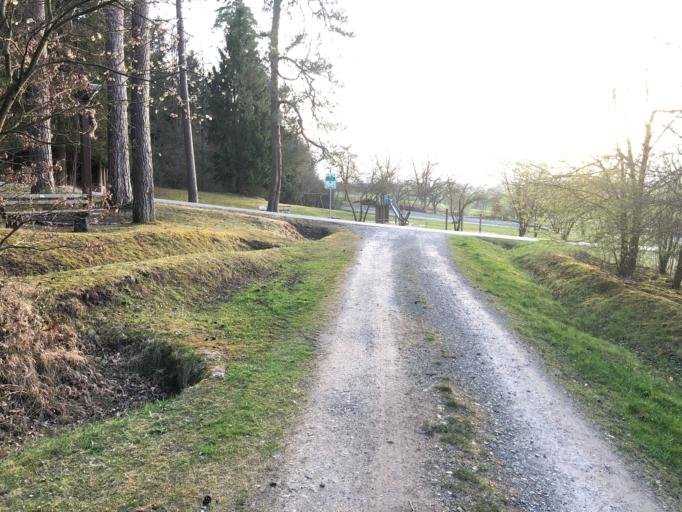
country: DE
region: Baden-Wuerttemberg
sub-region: Tuebingen Region
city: Rottenburg
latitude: 48.4302
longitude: 8.9414
